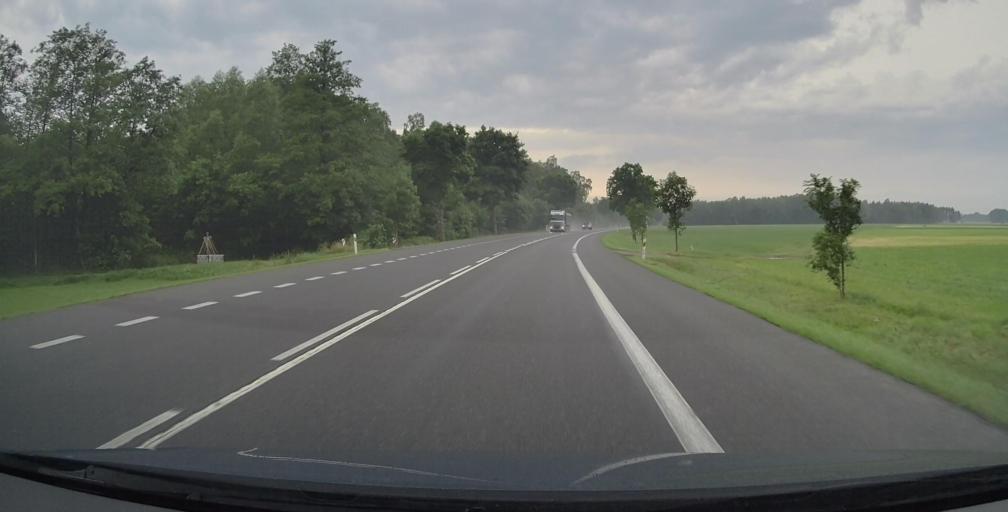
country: PL
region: Masovian Voivodeship
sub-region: Powiat siedlecki
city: Zbuczyn
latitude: 52.0767
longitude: 22.4919
